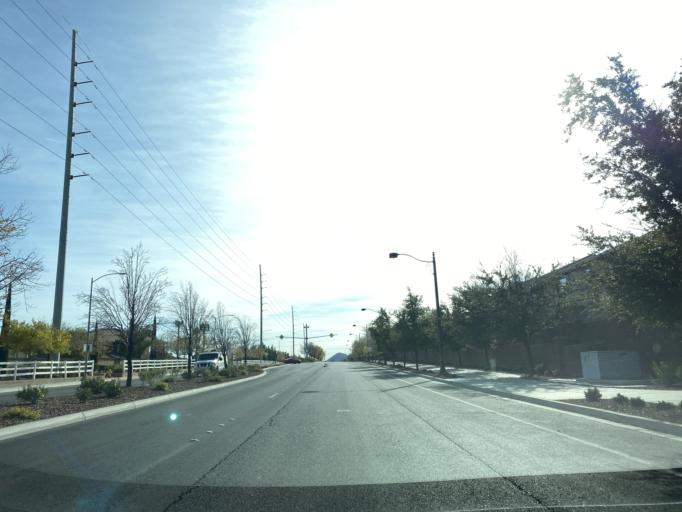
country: US
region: Nevada
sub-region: Clark County
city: Summerlin South
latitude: 36.3042
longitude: -115.3150
